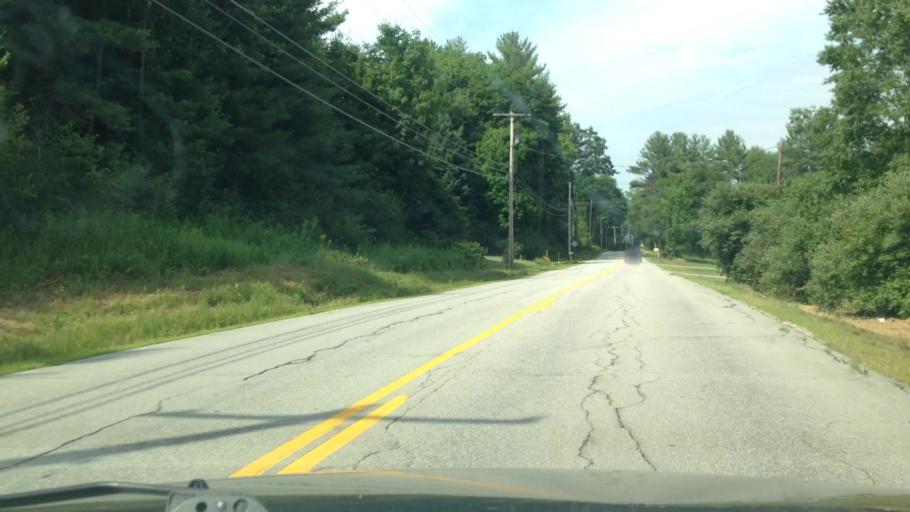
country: US
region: New Hampshire
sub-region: Cheshire County
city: Swanzey
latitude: 42.8596
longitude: -72.2477
